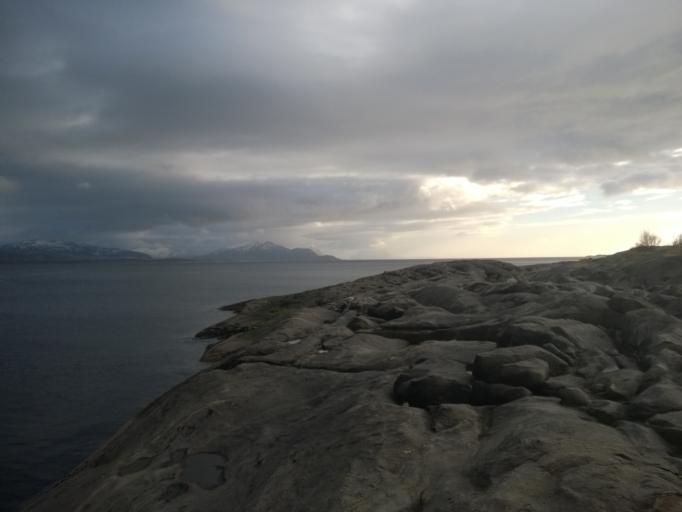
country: NO
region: Nordland
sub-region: Bodo
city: Lopsmarka
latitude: 67.2747
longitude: 14.5057
